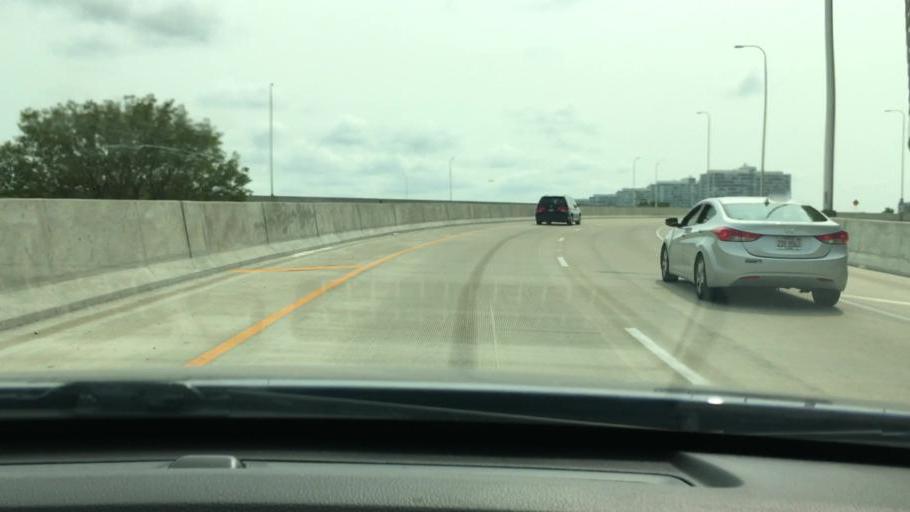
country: US
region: Illinois
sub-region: Cook County
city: Chicago
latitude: 41.8497
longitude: -87.6135
